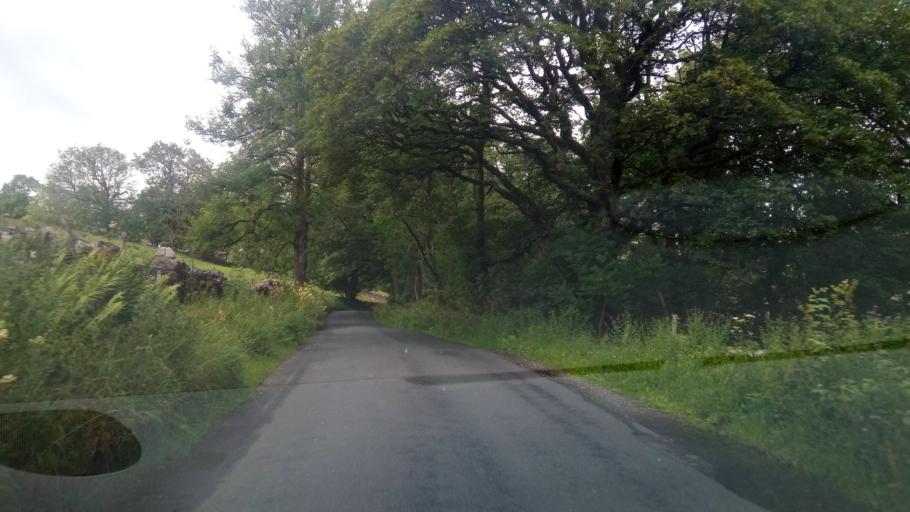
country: GB
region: England
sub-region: North Yorkshire
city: Ingleton
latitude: 54.2742
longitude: -2.3619
